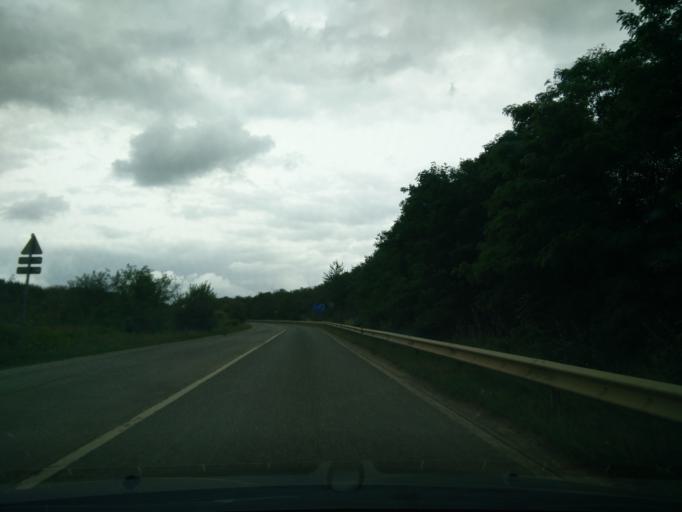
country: BE
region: Wallonia
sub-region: Province de Liege
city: Bassenge
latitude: 50.7872
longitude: 5.6393
